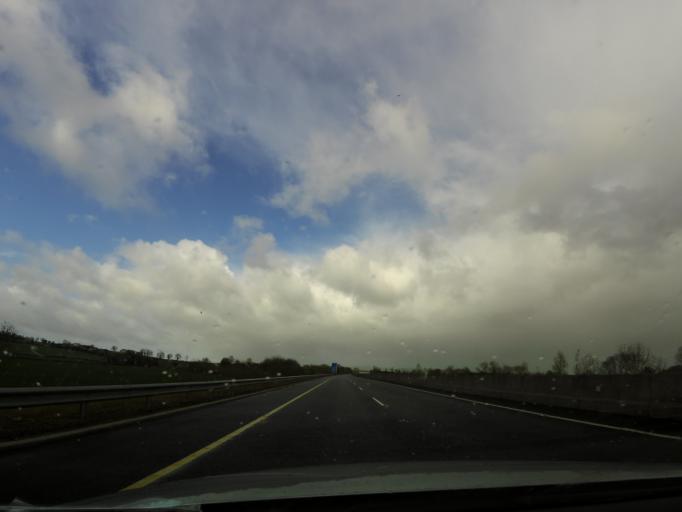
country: IE
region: Munster
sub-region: North Tipperary
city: Nenagh
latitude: 52.8444
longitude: -8.2171
